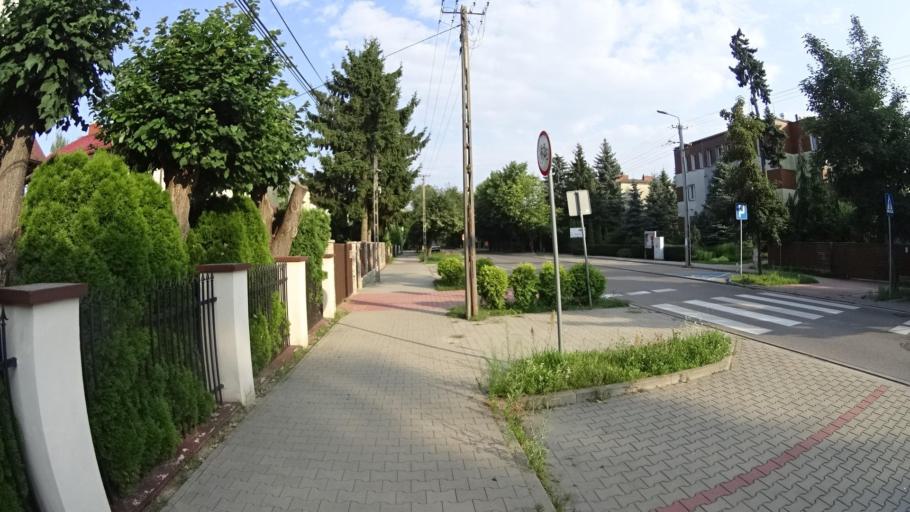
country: PL
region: Masovian Voivodeship
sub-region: Powiat pruszkowski
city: Michalowice
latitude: 52.1710
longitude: 20.8860
